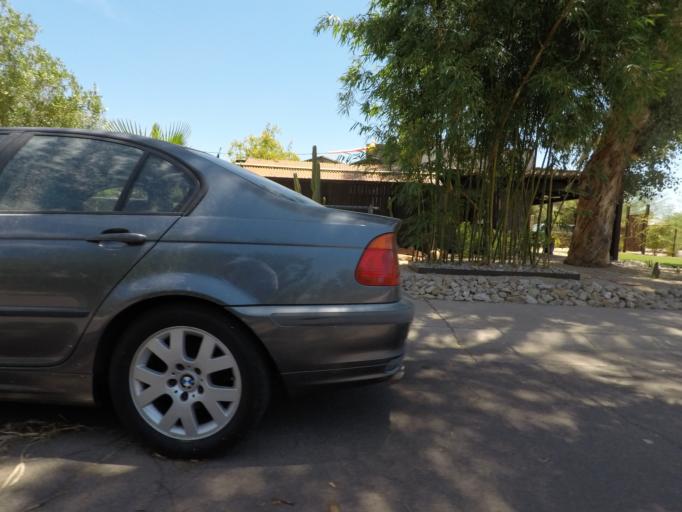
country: US
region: Arizona
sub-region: Maricopa County
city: Tempe Junction
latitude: 33.4162
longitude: -111.9457
